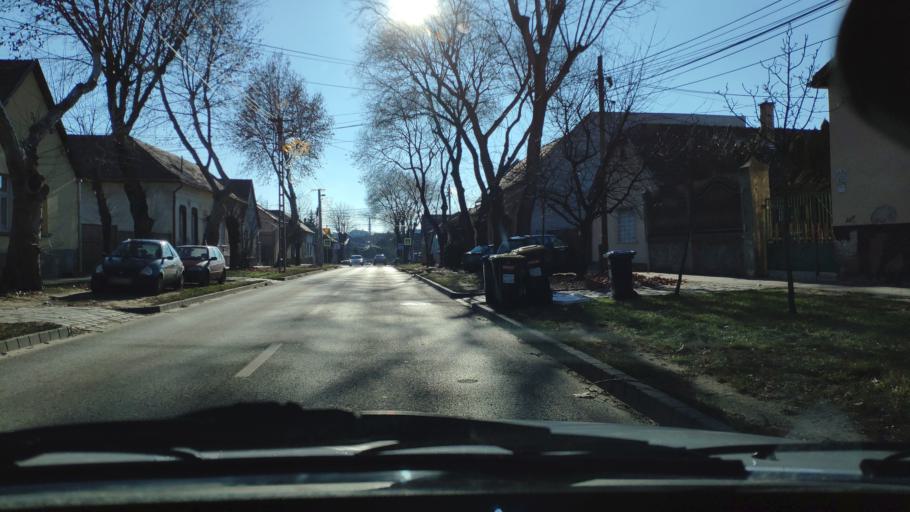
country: HU
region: Budapest
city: Budapest XXIII. keruelet
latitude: 47.3979
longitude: 19.1173
